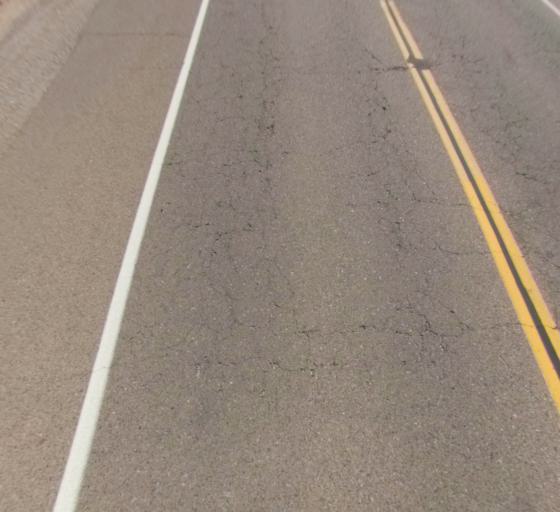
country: US
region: California
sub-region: Fresno County
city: Biola
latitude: 36.8501
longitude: -120.0779
